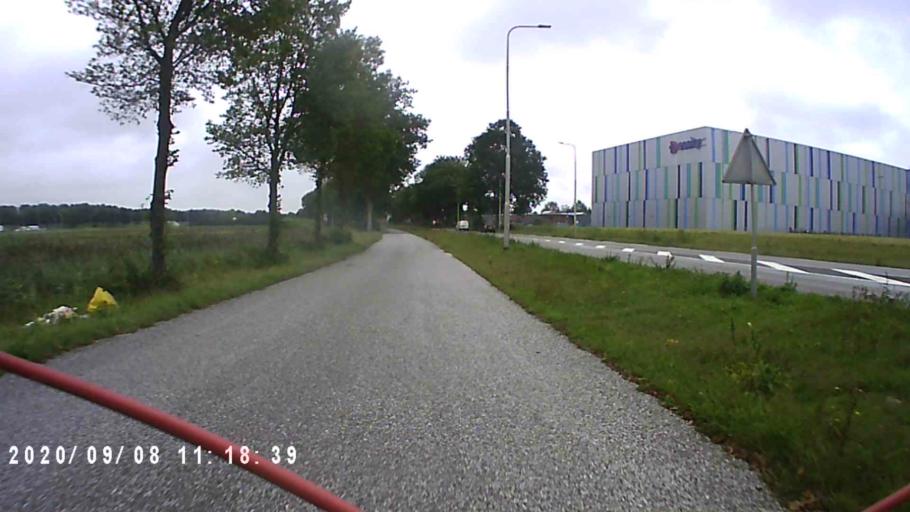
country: NL
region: Groningen
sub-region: Gemeente Hoogezand-Sappemeer
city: Hoogezand
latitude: 53.1688
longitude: 6.7445
